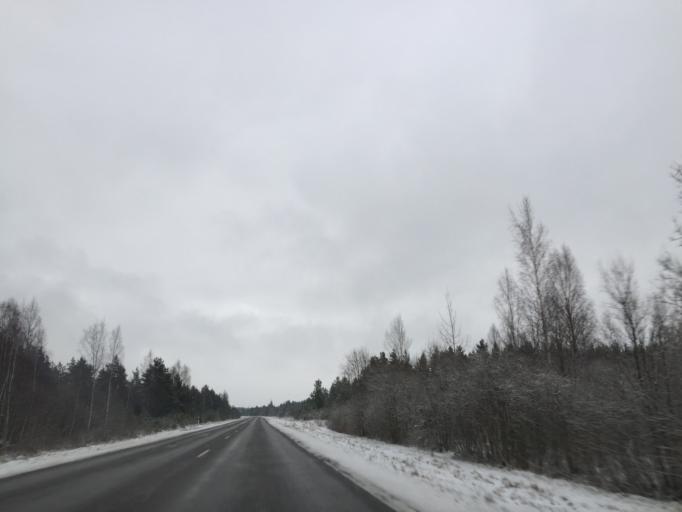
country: EE
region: Laeaene
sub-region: Lihula vald
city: Lihula
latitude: 58.6161
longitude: 23.9144
